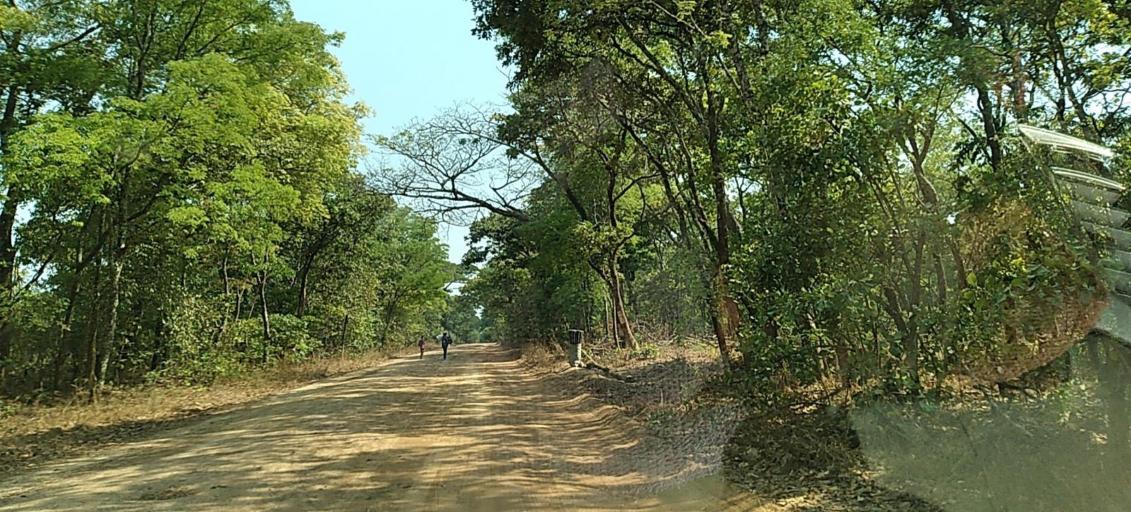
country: ZM
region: Copperbelt
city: Kalulushi
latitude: -12.9112
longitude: 27.8232
